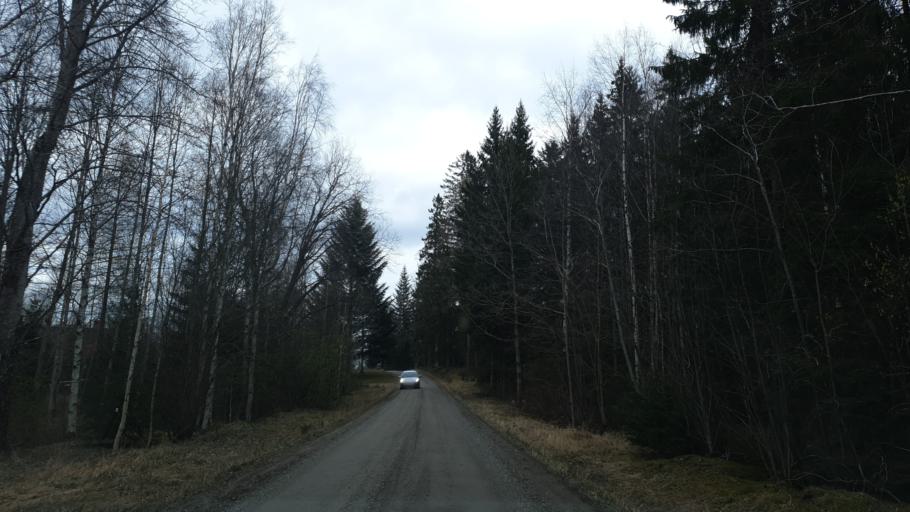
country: SE
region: OErebro
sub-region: Nora Kommun
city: As
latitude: 59.5968
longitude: 14.9111
